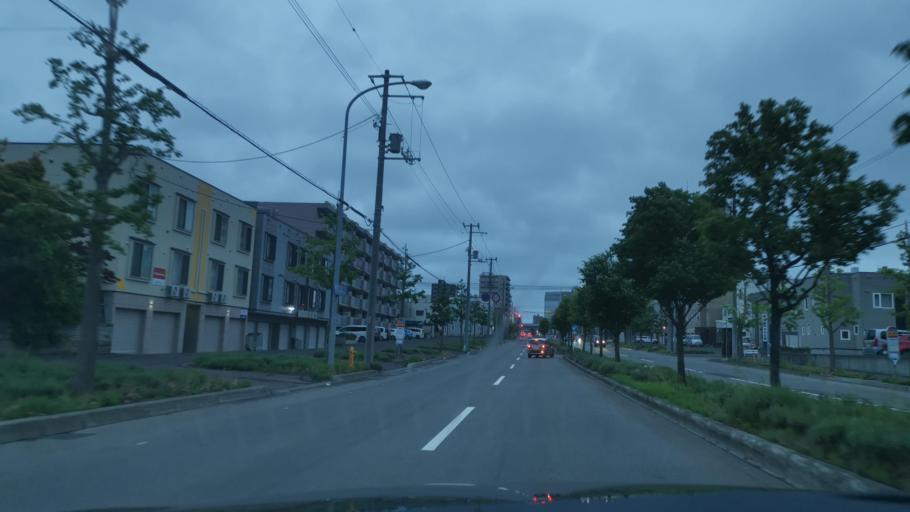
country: JP
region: Hokkaido
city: Sapporo
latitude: 43.0960
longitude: 141.2669
